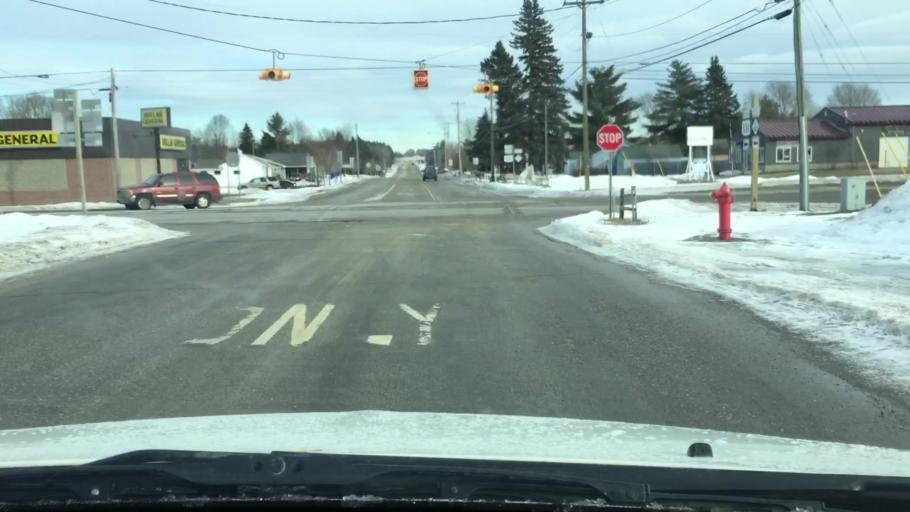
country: US
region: Michigan
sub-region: Wexford County
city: Manton
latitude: 44.4037
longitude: -85.3987
